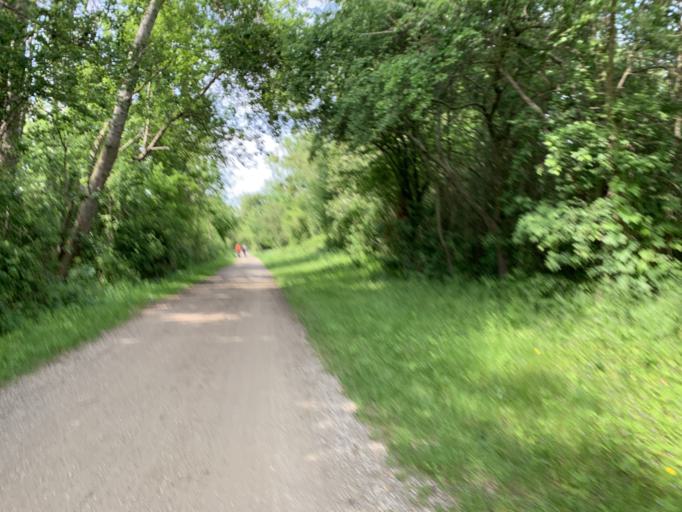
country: DE
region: North Rhine-Westphalia
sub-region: Regierungsbezirk Koln
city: Dueren
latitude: 50.7796
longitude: 6.4833
